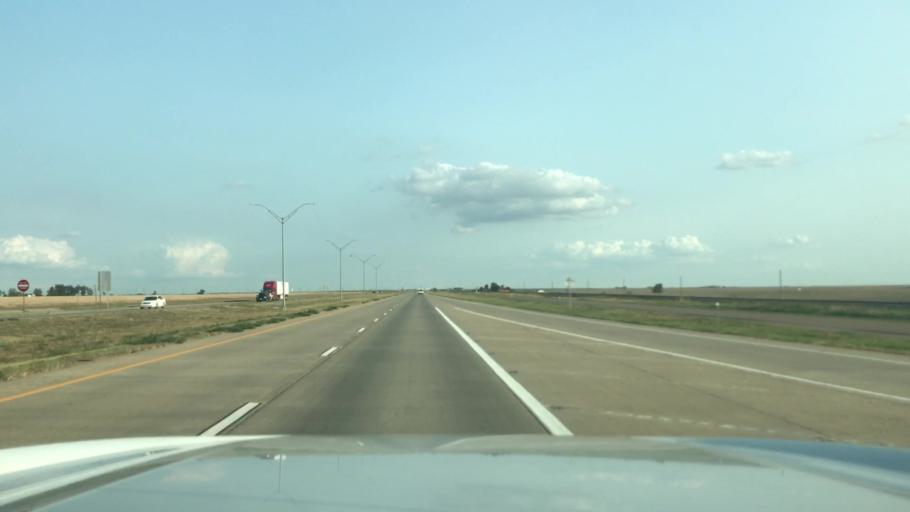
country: US
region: Texas
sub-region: Swisher County
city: Tulia
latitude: 34.6302
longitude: -101.8188
